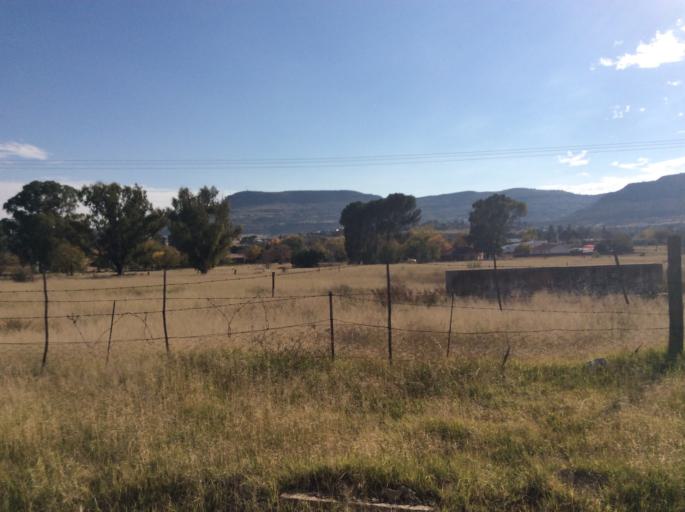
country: LS
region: Mafeteng
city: Mafeteng
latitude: -29.7342
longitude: 27.0297
